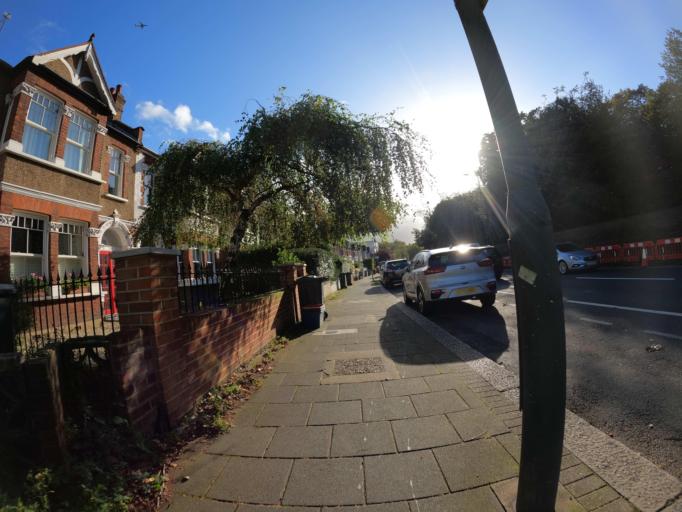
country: GB
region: England
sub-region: Greater London
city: Hammersmith
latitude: 51.4842
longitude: -0.2555
